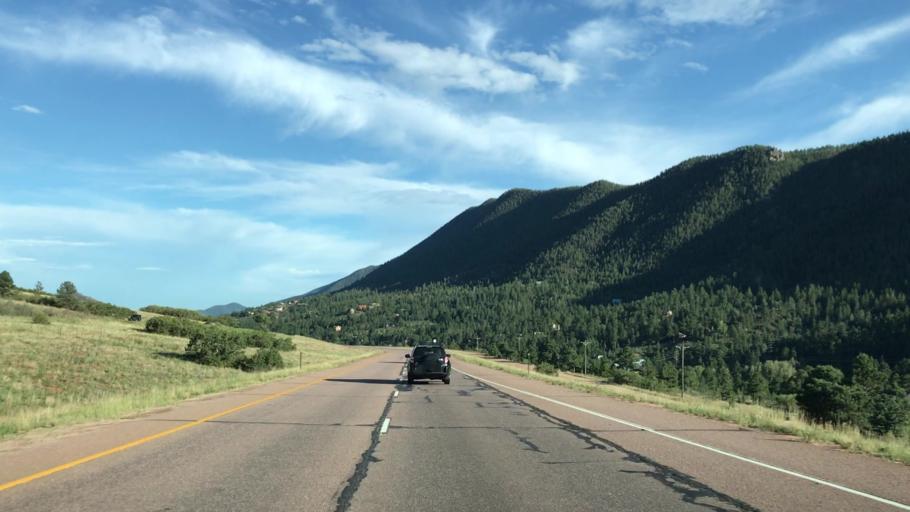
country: US
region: Colorado
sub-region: El Paso County
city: Cascade-Chipita Park
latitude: 38.9289
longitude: -104.9994
